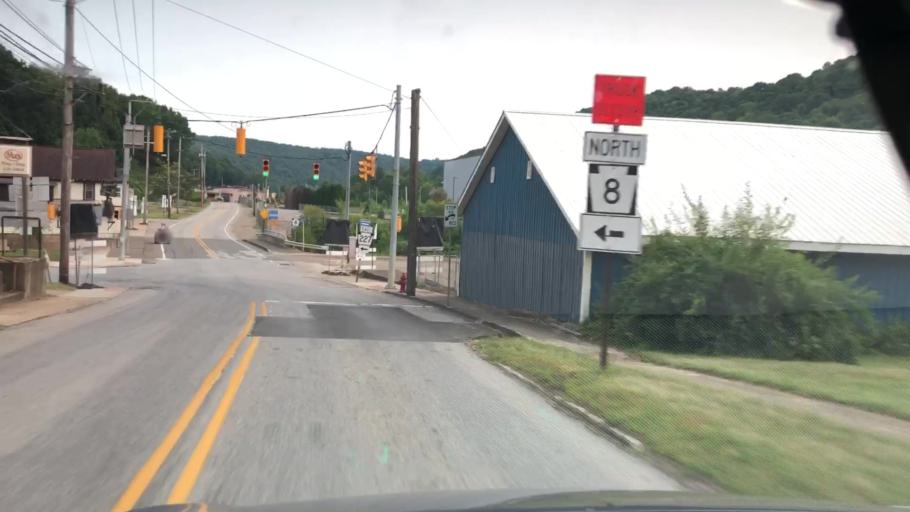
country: US
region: Pennsylvania
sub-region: Venango County
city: Hasson Heights
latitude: 41.4695
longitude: -79.6918
